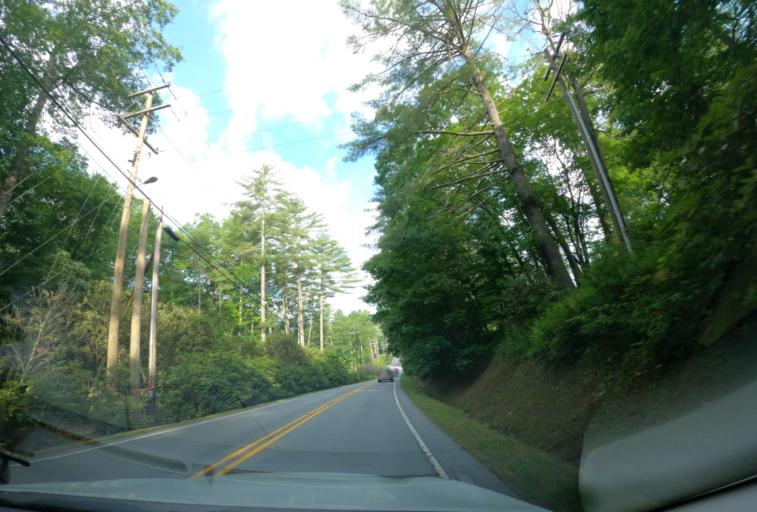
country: US
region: North Carolina
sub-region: Jackson County
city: Cullowhee
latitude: 35.1123
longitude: -83.0251
